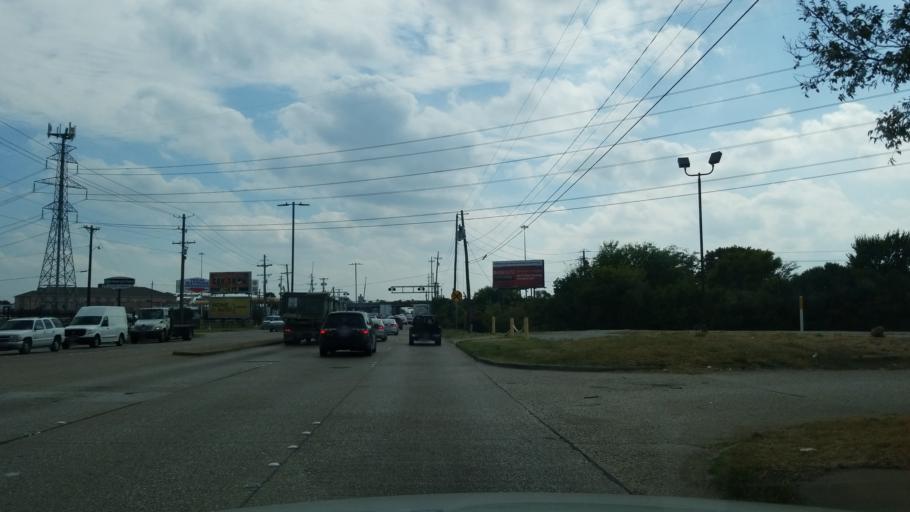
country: US
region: Texas
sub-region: Dallas County
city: Garland
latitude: 32.8778
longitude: -96.6832
